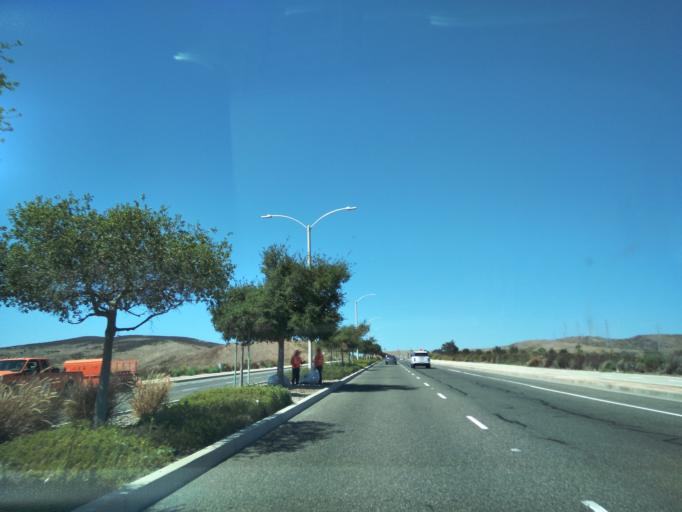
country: US
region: California
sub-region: Orange County
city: San Clemente
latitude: 33.4660
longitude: -117.6061
